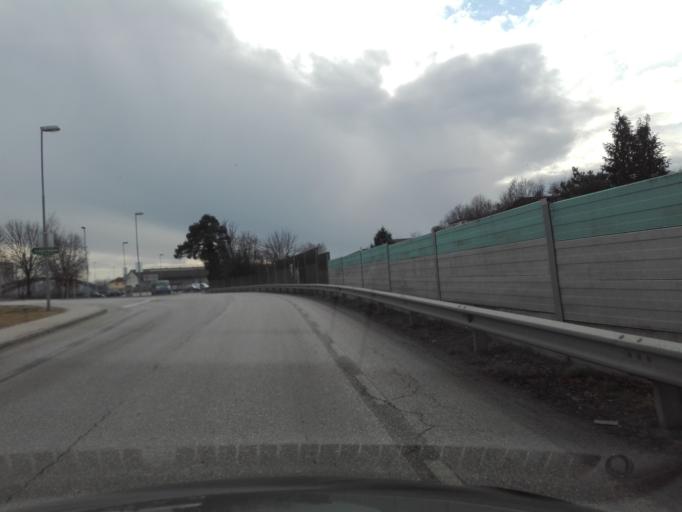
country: AT
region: Upper Austria
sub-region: Politischer Bezirk Perg
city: Perg
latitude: 48.2712
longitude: 14.5771
